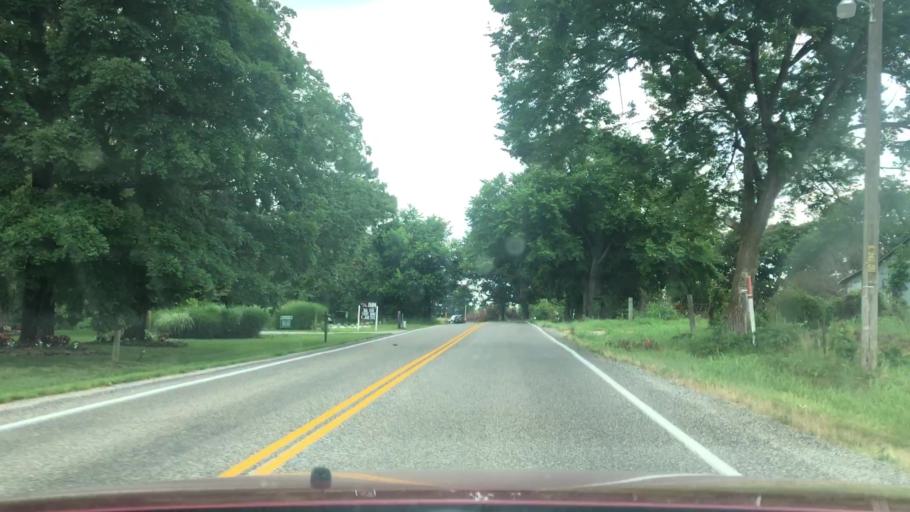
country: US
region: Missouri
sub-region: Christian County
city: Ozark
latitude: 36.9435
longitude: -93.2369
